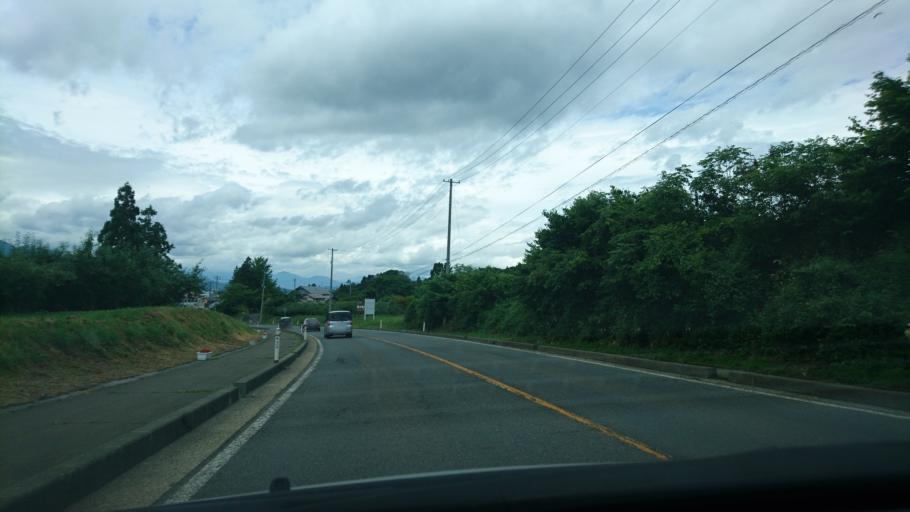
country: JP
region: Iwate
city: Morioka-shi
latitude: 39.6145
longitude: 141.1982
